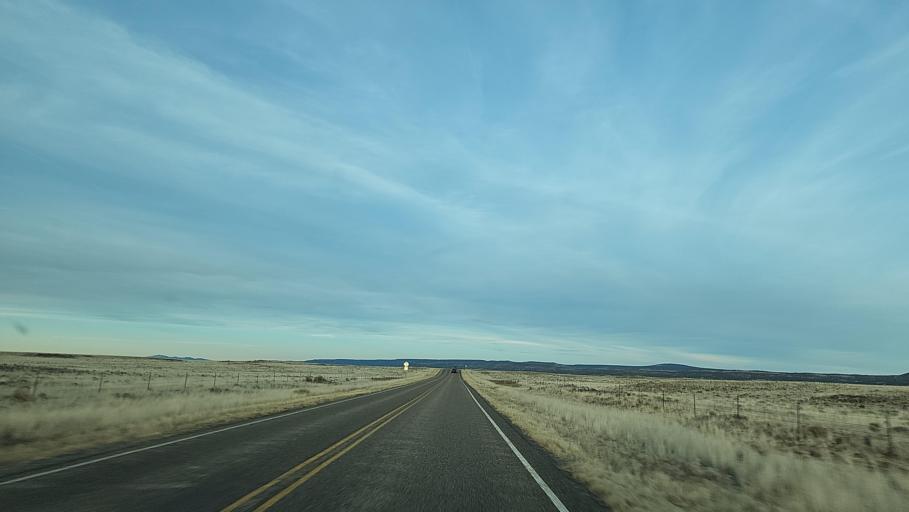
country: US
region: New Mexico
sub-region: Cibola County
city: Grants
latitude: 34.6826
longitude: -108.0734
